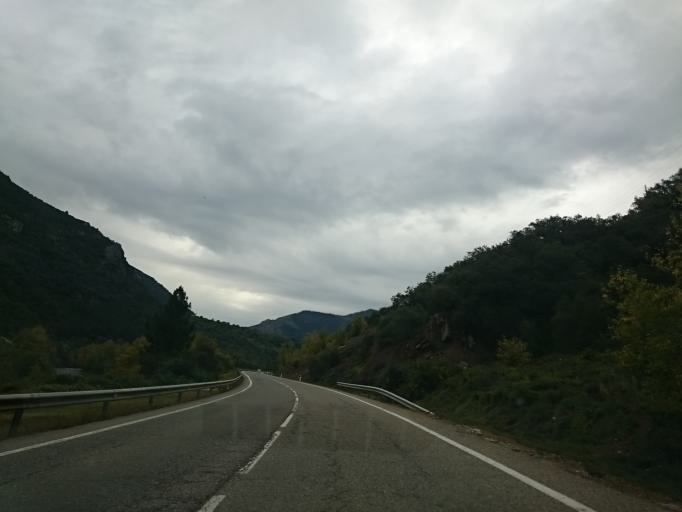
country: ES
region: Catalonia
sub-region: Provincia de Lleida
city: Sort
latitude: 42.3658
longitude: 1.0979
